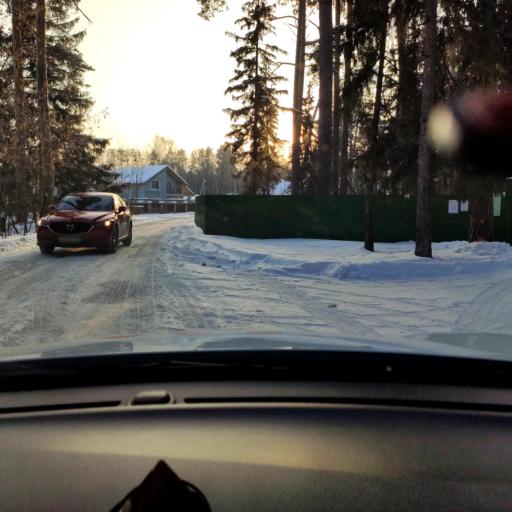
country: RU
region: Tatarstan
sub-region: Zelenodol'skiy Rayon
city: Vasil'yevo
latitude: 55.9098
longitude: 48.7475
